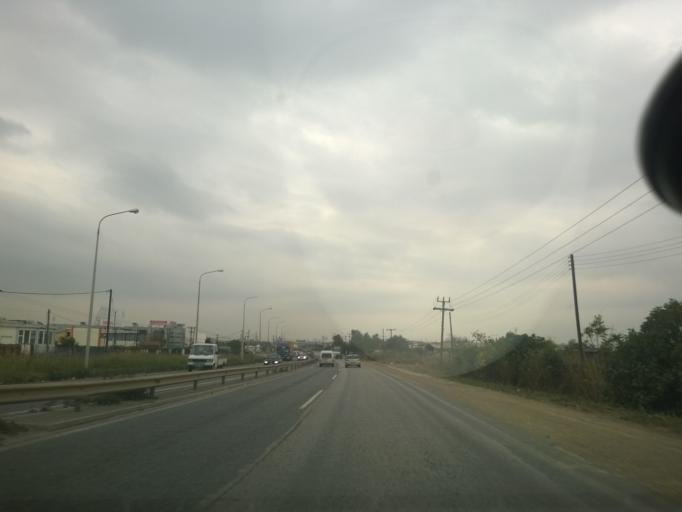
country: GR
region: Central Macedonia
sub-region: Nomos Thessalonikis
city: Sindos
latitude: 40.7058
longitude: 22.8064
